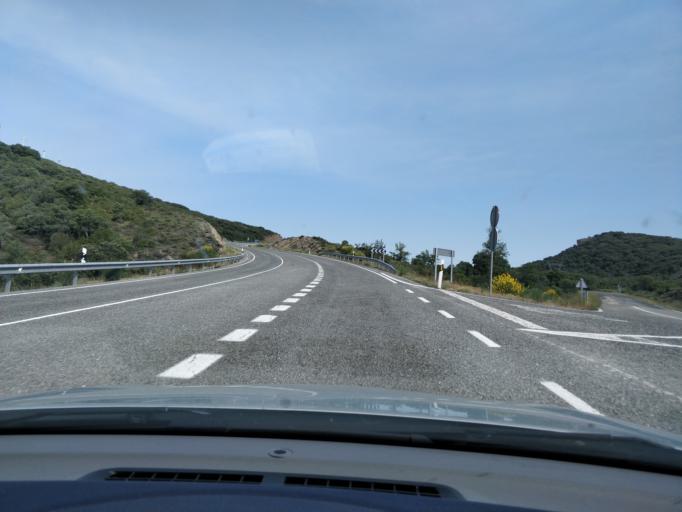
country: ES
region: Castille and Leon
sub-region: Provincia de Burgos
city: Medina de Pomar
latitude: 42.9140
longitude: -3.6085
